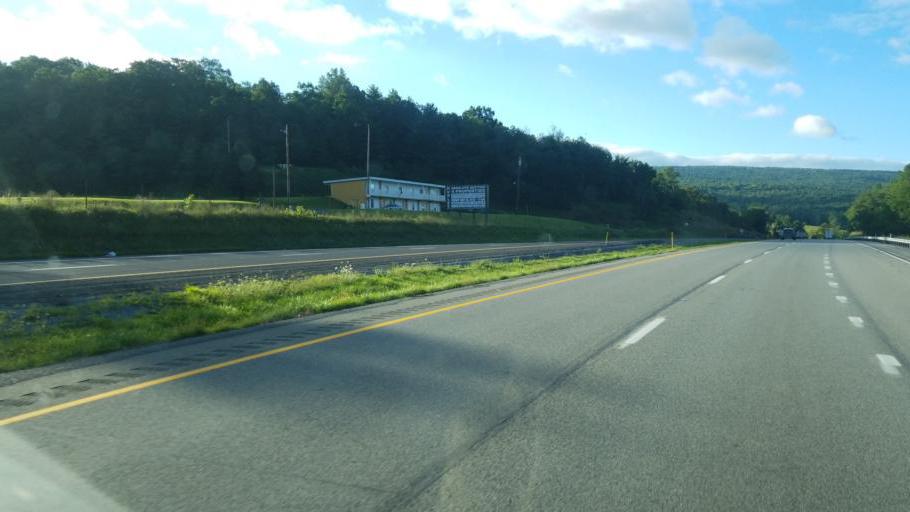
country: US
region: Pennsylvania
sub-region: Bedford County
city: Earlston
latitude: 39.9467
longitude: -78.2289
